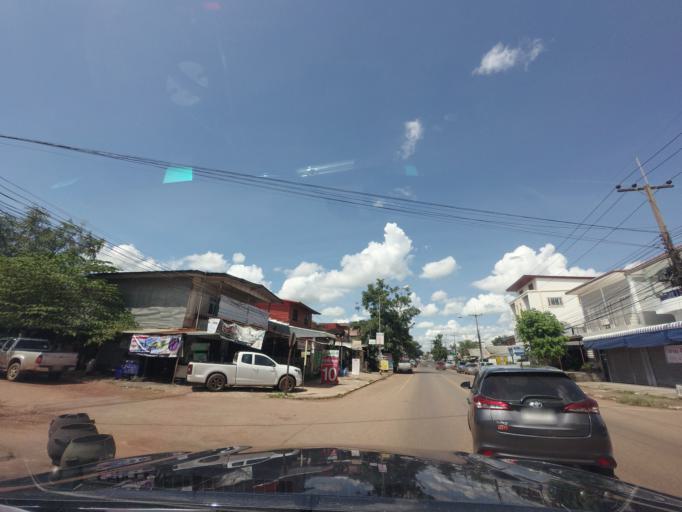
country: TH
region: Changwat Udon Thani
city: Ban Dung
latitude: 17.6939
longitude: 103.2581
